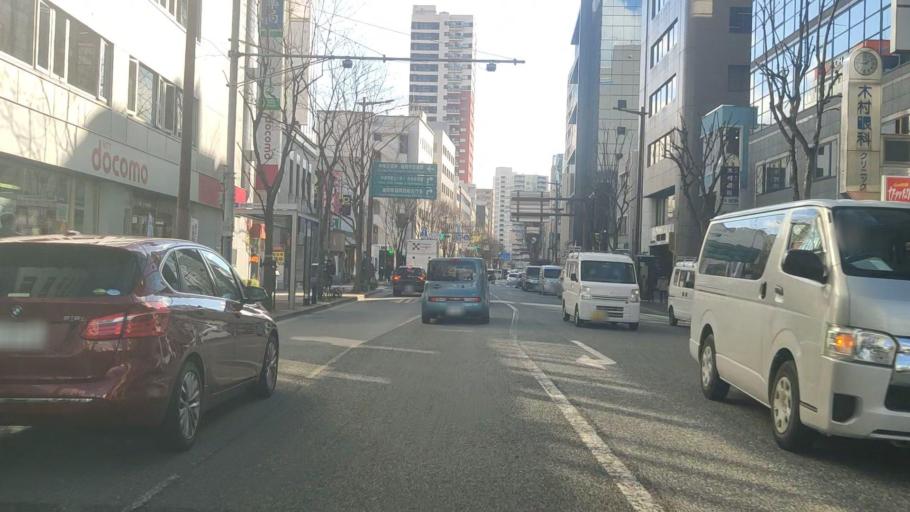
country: JP
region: Fukuoka
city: Fukuoka-shi
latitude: 33.5888
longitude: 130.3907
